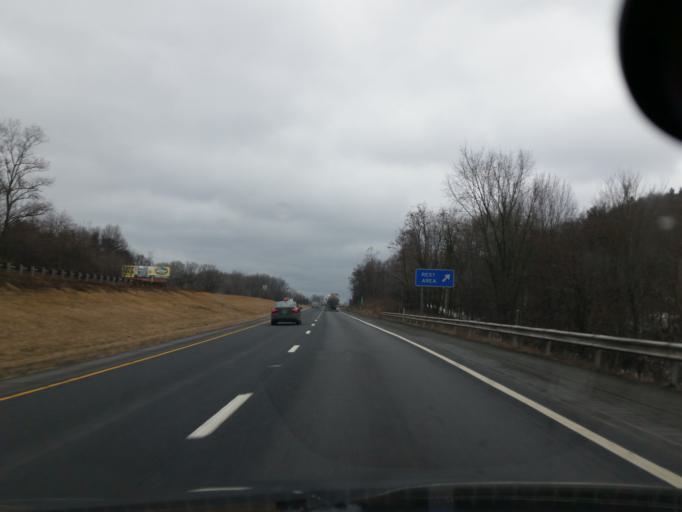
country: US
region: Pennsylvania
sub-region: Wyoming County
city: Factoryville
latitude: 41.6786
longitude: -75.6867
